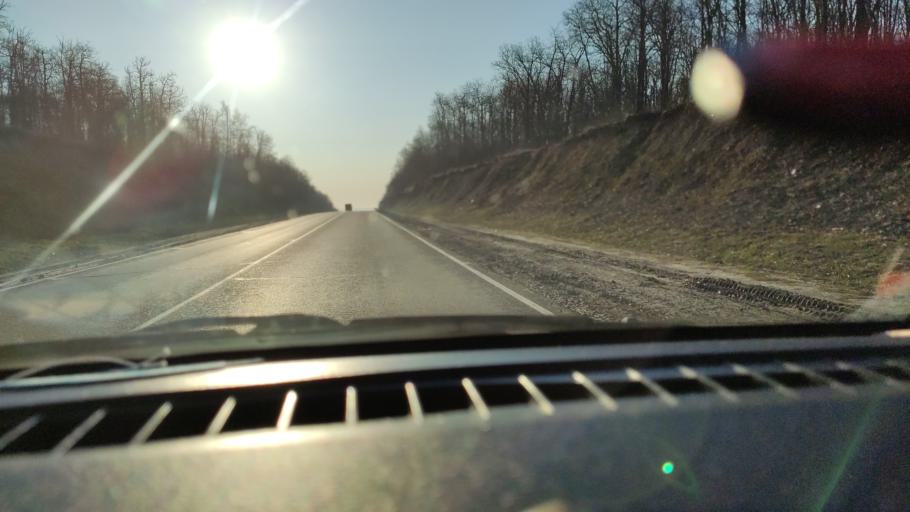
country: RU
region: Saratov
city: Vol'sk
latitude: 52.1079
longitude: 47.4002
